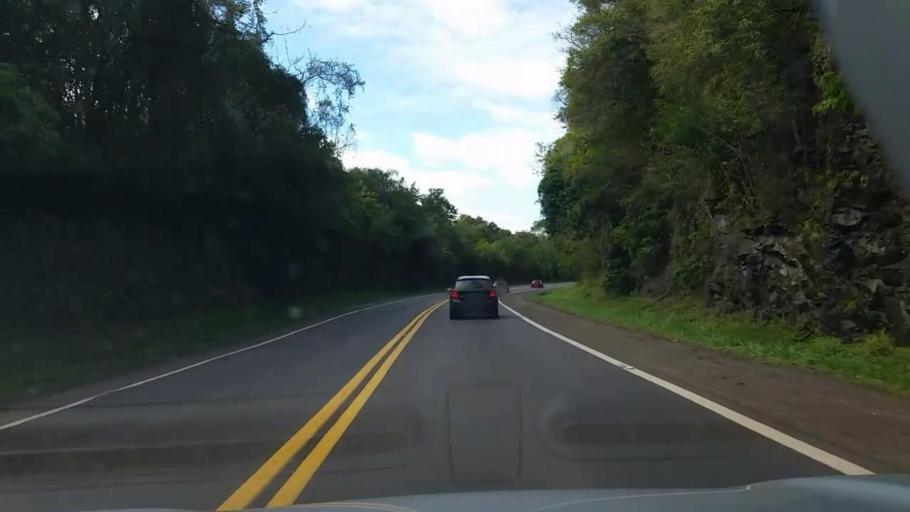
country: BR
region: Rio Grande do Sul
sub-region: Arroio Do Meio
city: Arroio do Meio
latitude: -29.3354
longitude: -52.0915
